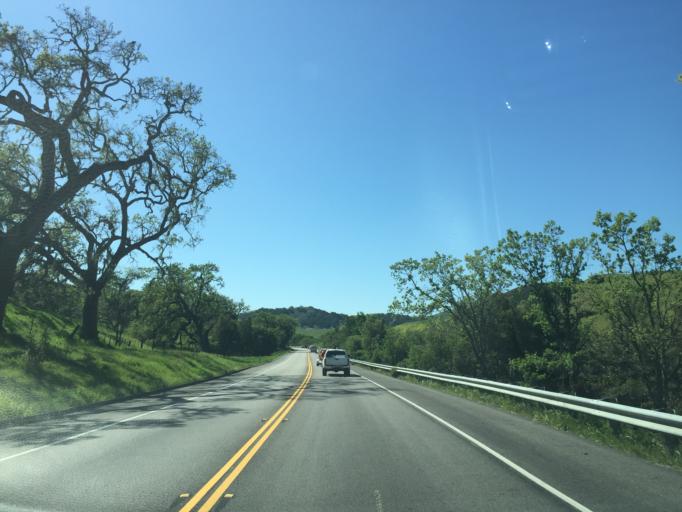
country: US
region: California
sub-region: Santa Barbara County
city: Los Olivos
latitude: 34.6822
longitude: -120.1440
